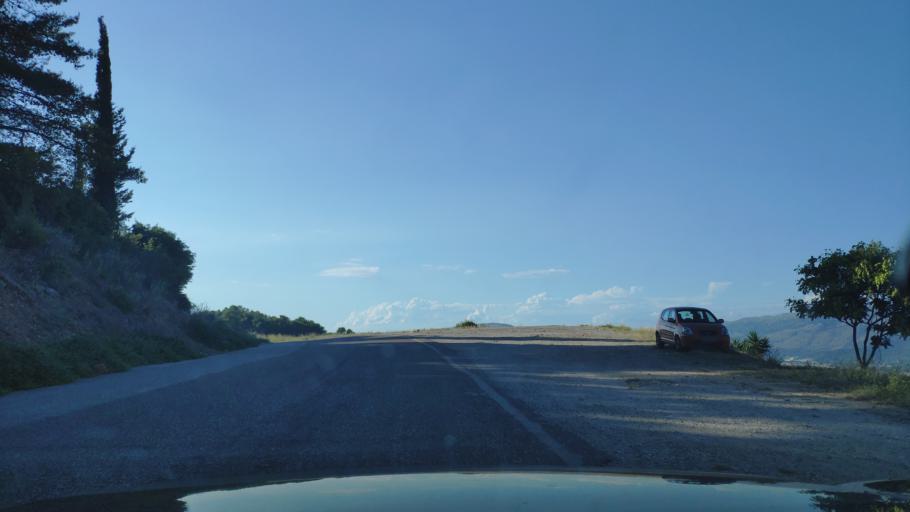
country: GR
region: West Greece
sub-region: Nomos Aitolias kai Akarnanias
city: Fitiai
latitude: 38.7010
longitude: 21.1865
